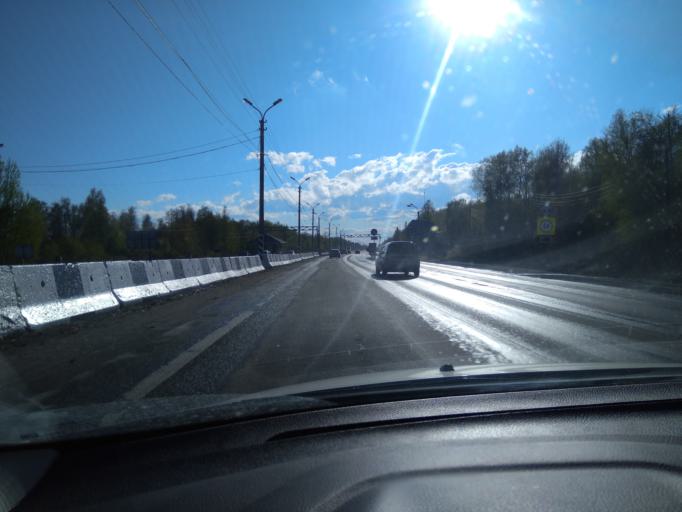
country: RU
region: Tjumen
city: Moskovskiy
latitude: 57.1139
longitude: 65.4123
